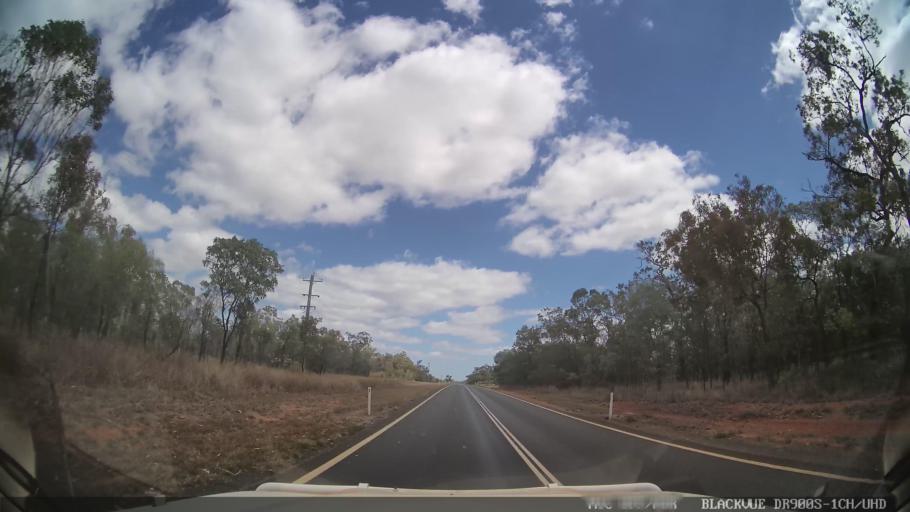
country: AU
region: Queensland
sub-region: Tablelands
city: Ravenshoe
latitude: -17.9096
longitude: 144.8809
